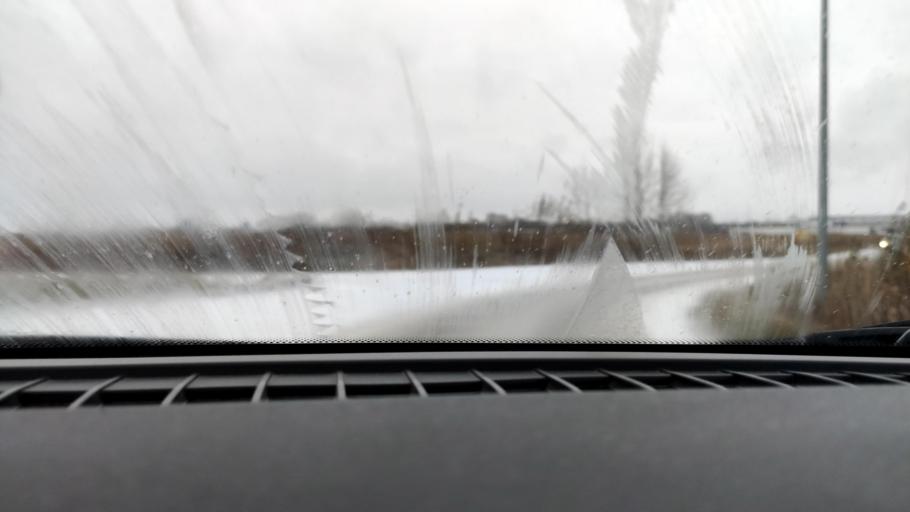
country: RU
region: Perm
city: Kondratovo
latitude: 57.9267
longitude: 56.1716
